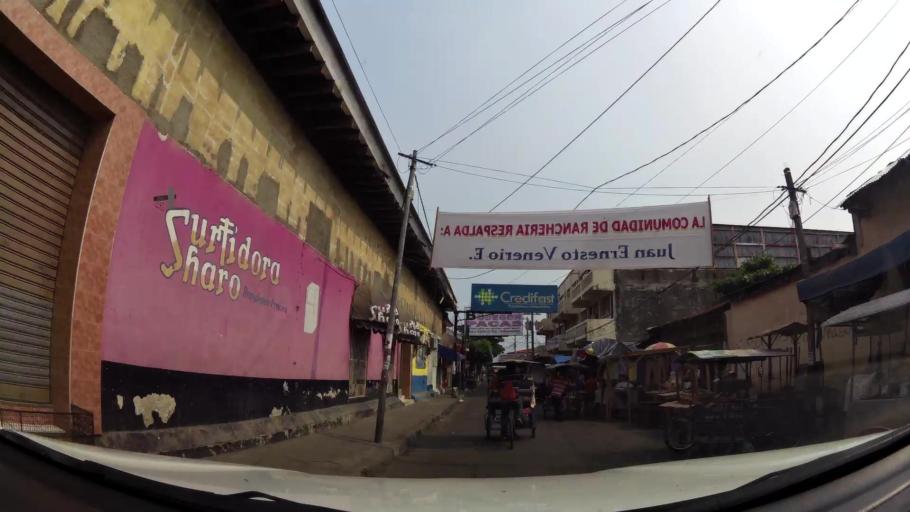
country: NI
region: Chinandega
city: Chinandega
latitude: 12.6304
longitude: -87.1293
